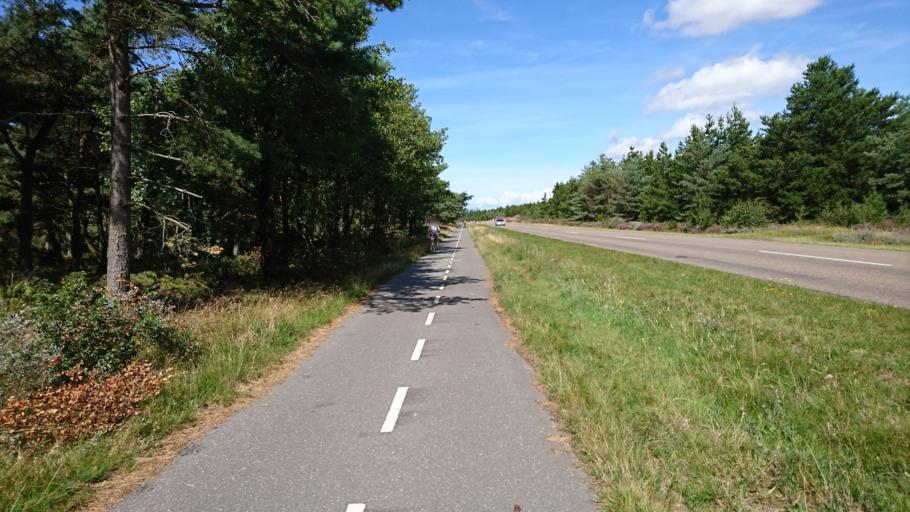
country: DK
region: South Denmark
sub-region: Fano Kommune
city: Nordby
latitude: 55.4023
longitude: 8.4205
